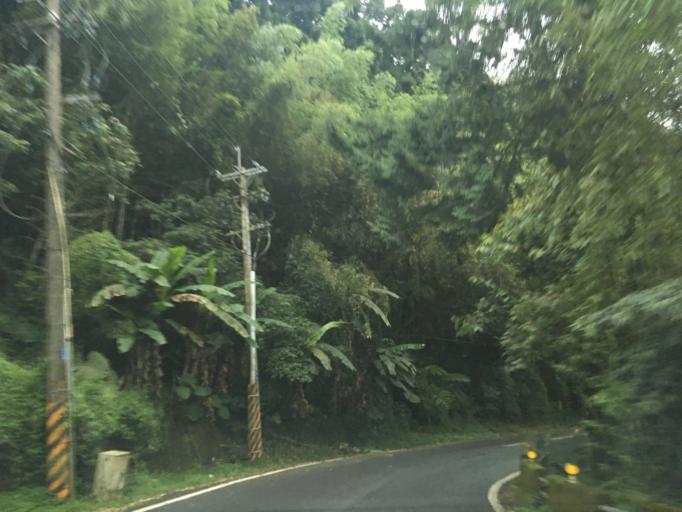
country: TW
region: Taiwan
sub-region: Chiayi
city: Jiayi Shi
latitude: 23.4831
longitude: 120.6965
